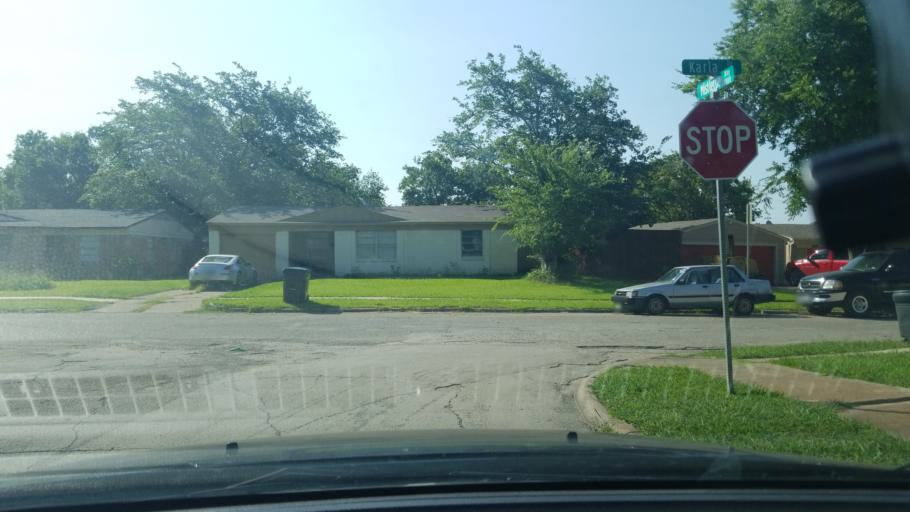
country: US
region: Texas
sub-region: Dallas County
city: Mesquite
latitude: 32.8293
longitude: -96.6460
